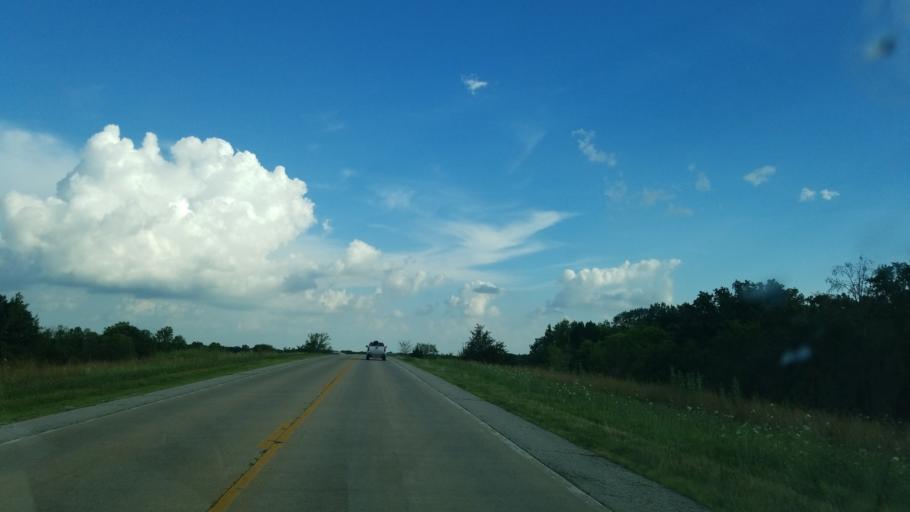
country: US
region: Illinois
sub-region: Marion County
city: Sandoval
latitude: 38.5827
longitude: -89.1084
